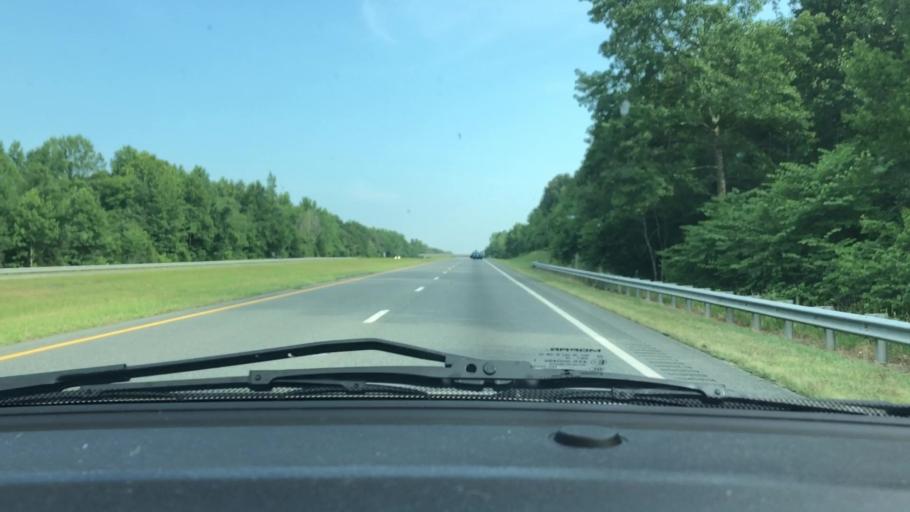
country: US
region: North Carolina
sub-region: Guilford County
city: Forest Oaks
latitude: 35.9407
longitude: -79.6868
